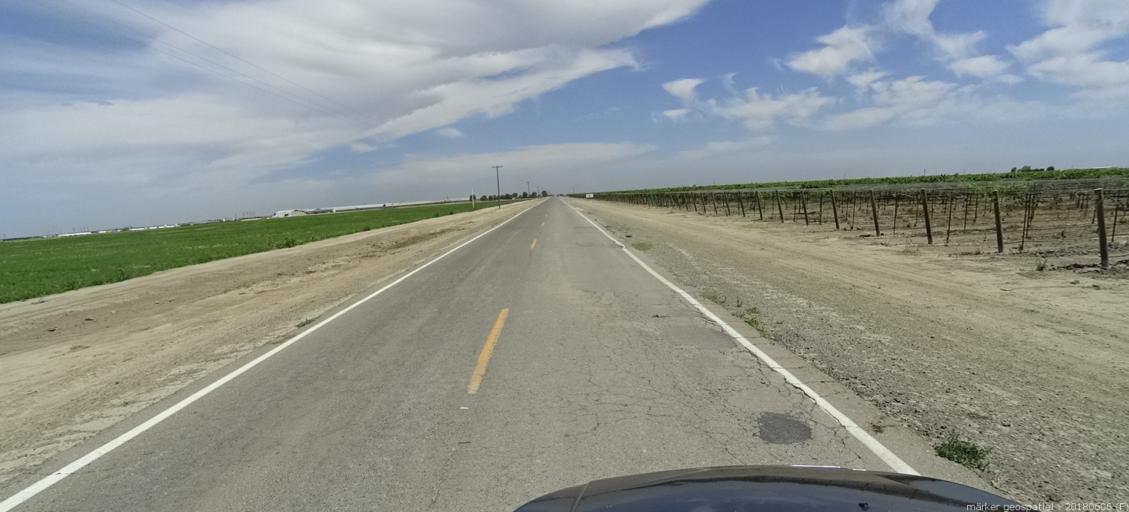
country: US
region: California
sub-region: Fresno County
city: Firebaugh
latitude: 36.9252
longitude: -120.3822
